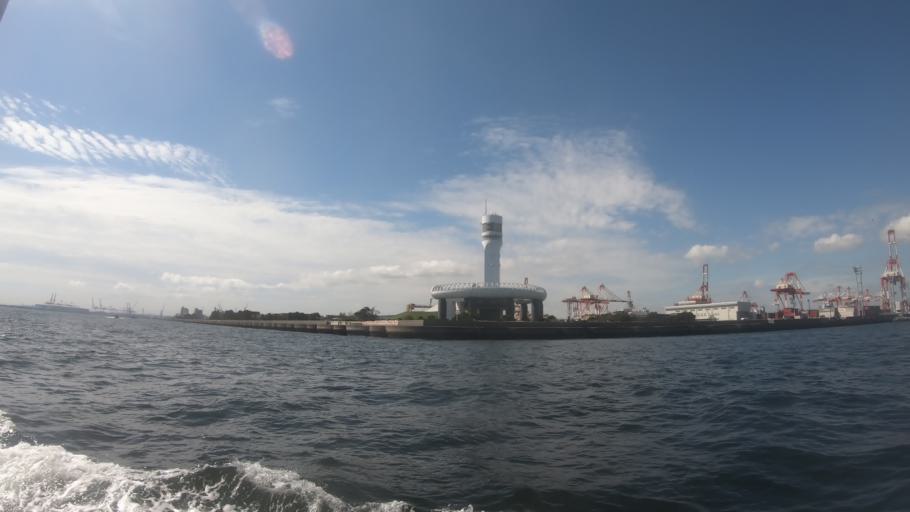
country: JP
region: Kanagawa
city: Yokohama
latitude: 35.4399
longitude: 139.6911
